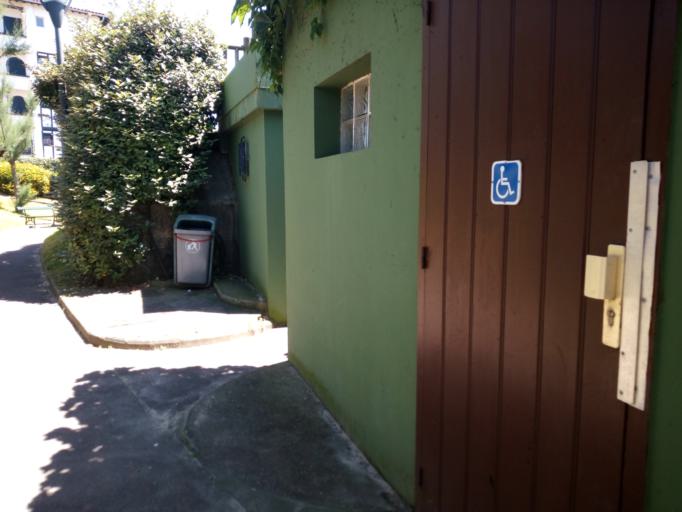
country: FR
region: Aquitaine
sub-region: Departement des Pyrenees-Atlantiques
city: Saint-Jean-de-Luz
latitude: 43.3875
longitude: -1.6679
